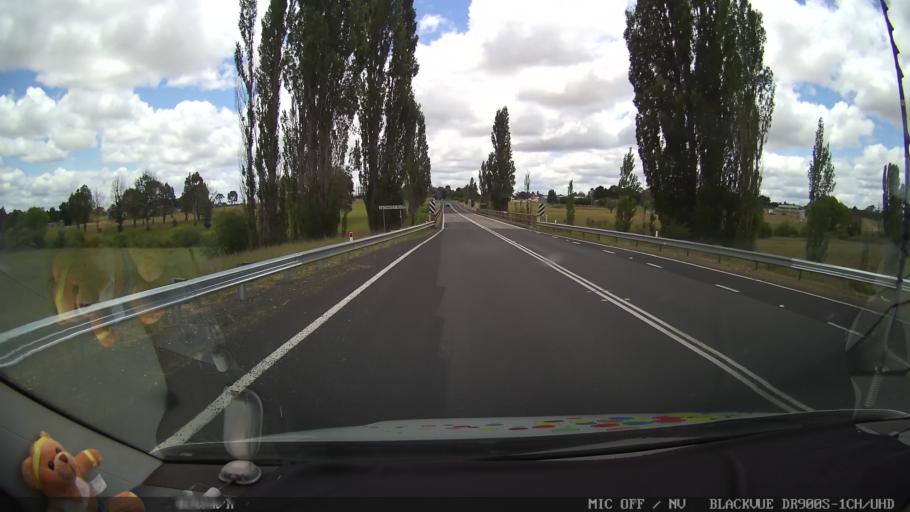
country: AU
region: New South Wales
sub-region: Glen Innes Severn
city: Glen Innes
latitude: -29.4464
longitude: 151.8429
